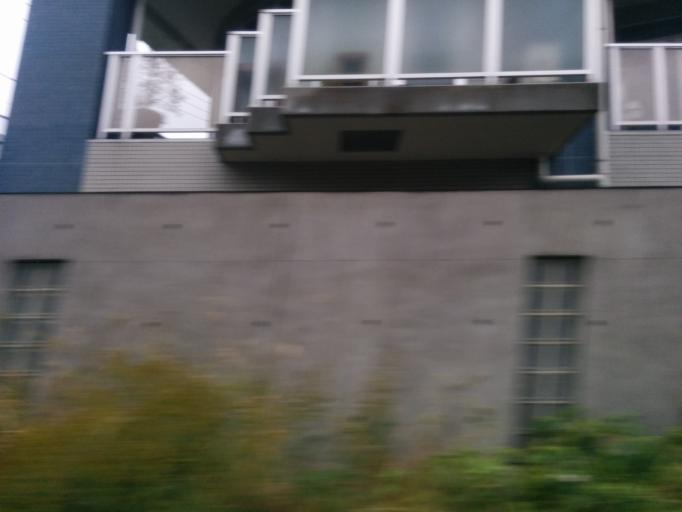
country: JP
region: Tokyo
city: Tokyo
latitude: 35.6812
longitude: 139.6954
